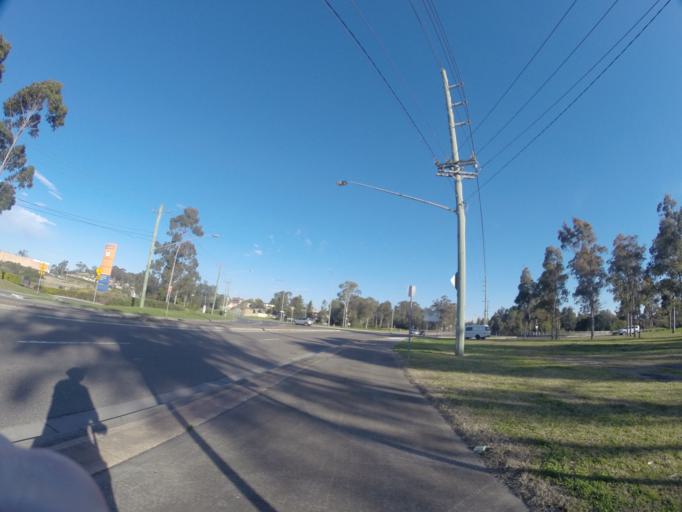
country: AU
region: New South Wales
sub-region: Fairfield
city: Horsley Park
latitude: -33.8504
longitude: 150.8765
